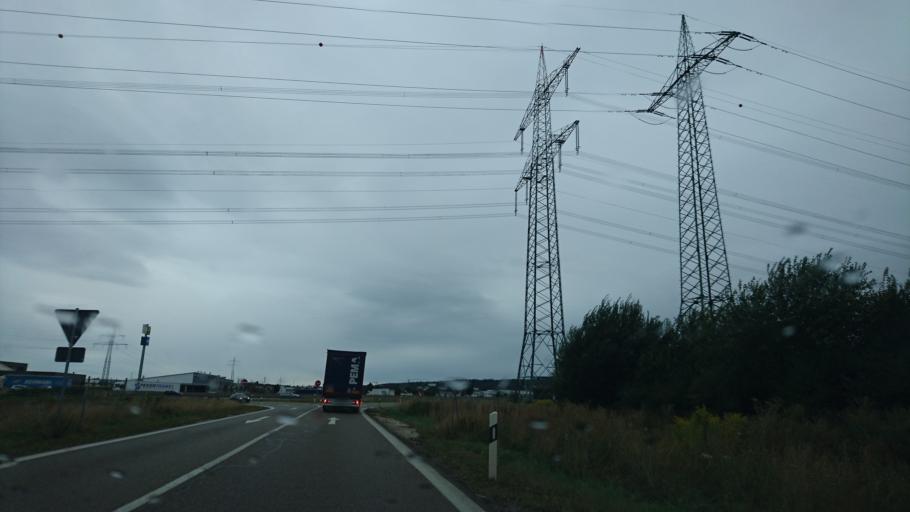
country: DE
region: Bavaria
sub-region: Swabia
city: Friedberg
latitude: 48.4032
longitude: 10.9519
